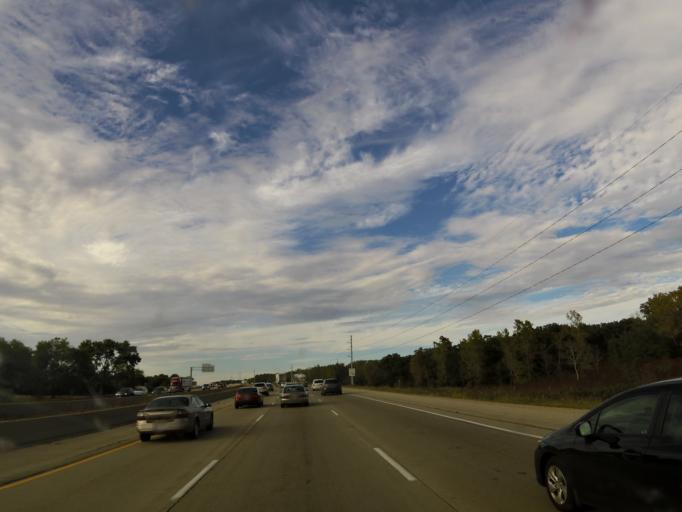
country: US
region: Wisconsin
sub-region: Dane County
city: McFarland
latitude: 43.0615
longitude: -89.2770
